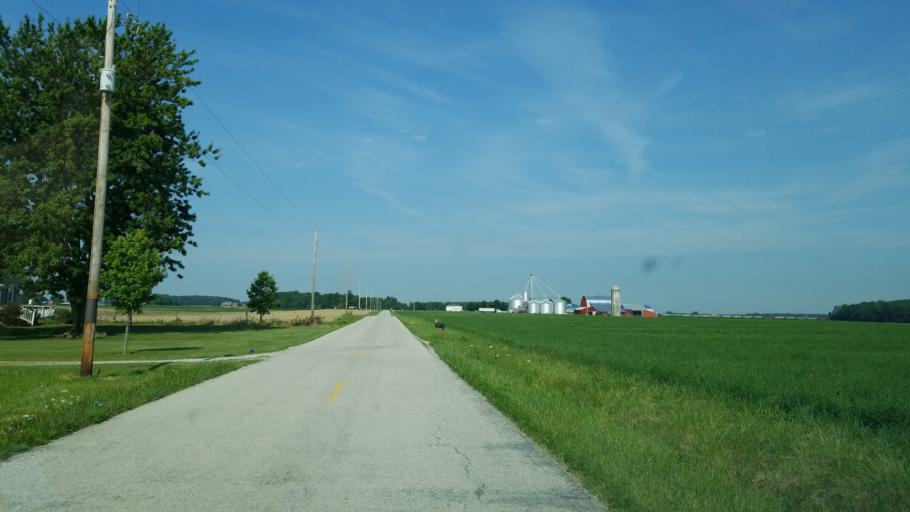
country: US
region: Ohio
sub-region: Huron County
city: Willard
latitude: 41.0227
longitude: -82.8884
